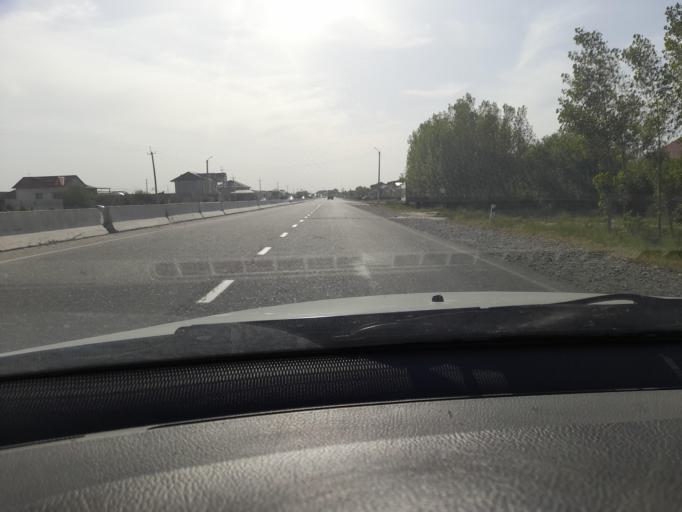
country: UZ
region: Samarqand
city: Kattaqo'rg'on
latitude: 39.9286
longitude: 66.2553
